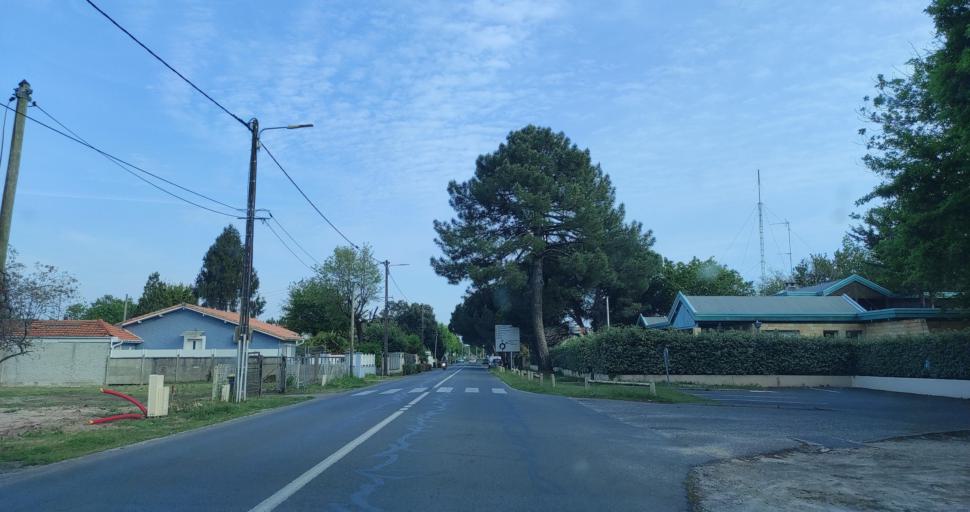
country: FR
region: Aquitaine
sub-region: Departement de la Gironde
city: Andernos-les-Bains
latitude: 44.7507
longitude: -1.1086
